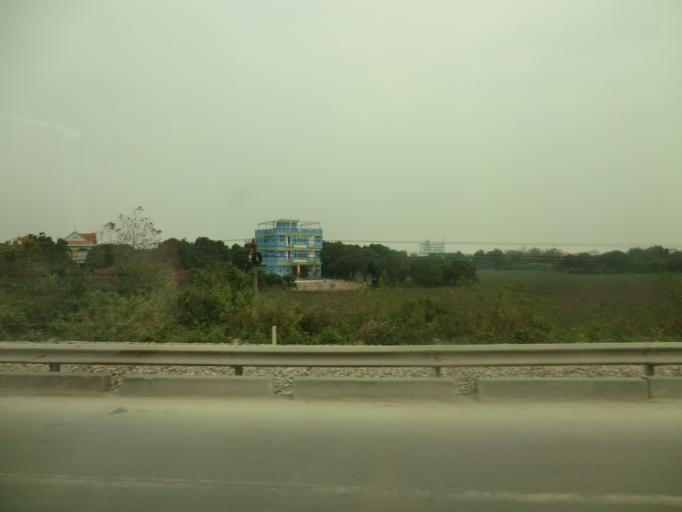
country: VN
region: Ha Nam
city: Thanh Pho Phu Ly
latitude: 20.5540
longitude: 105.9183
